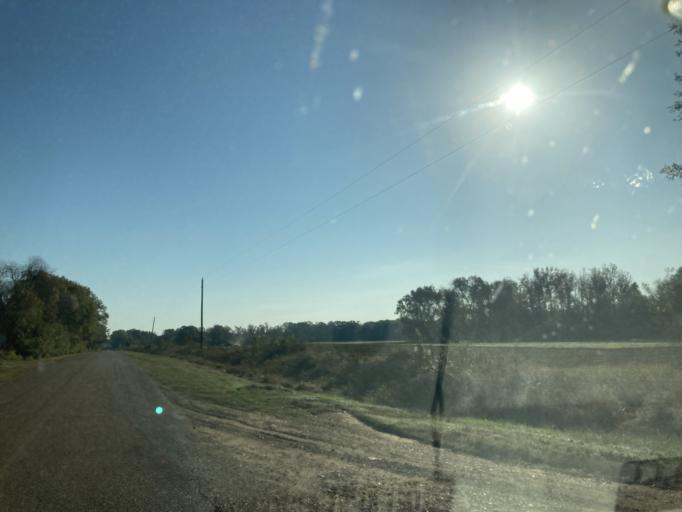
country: US
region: Mississippi
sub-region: Madison County
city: Kearney Park
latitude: 32.7130
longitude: -90.1927
